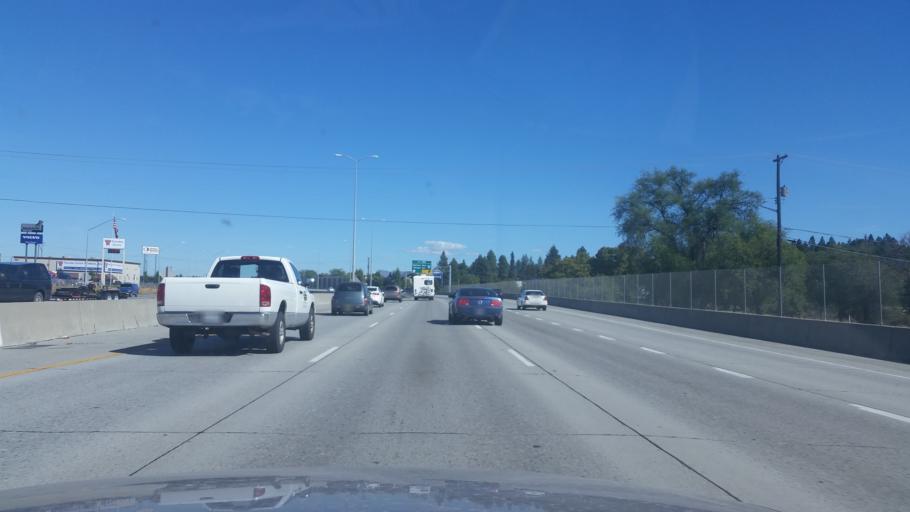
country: US
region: Washington
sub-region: Spokane County
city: Dishman
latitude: 47.6537
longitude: -117.3310
